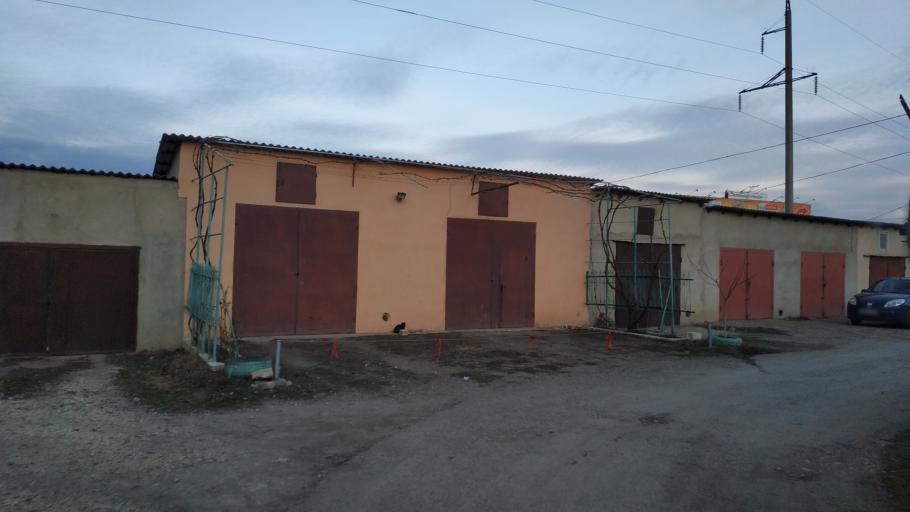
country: MD
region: Hincesti
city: Hincesti
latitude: 46.8329
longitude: 28.5951
